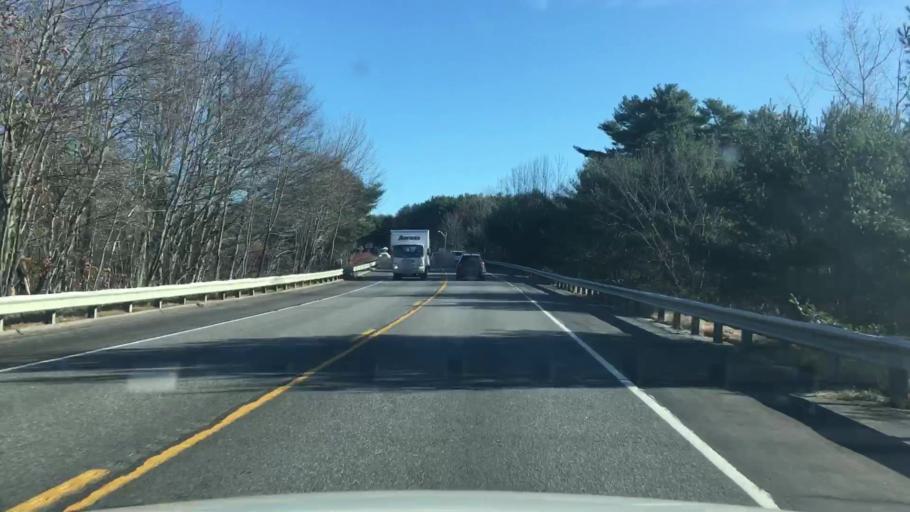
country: US
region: Maine
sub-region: Knox County
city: Union
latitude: 44.2123
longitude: -69.2260
